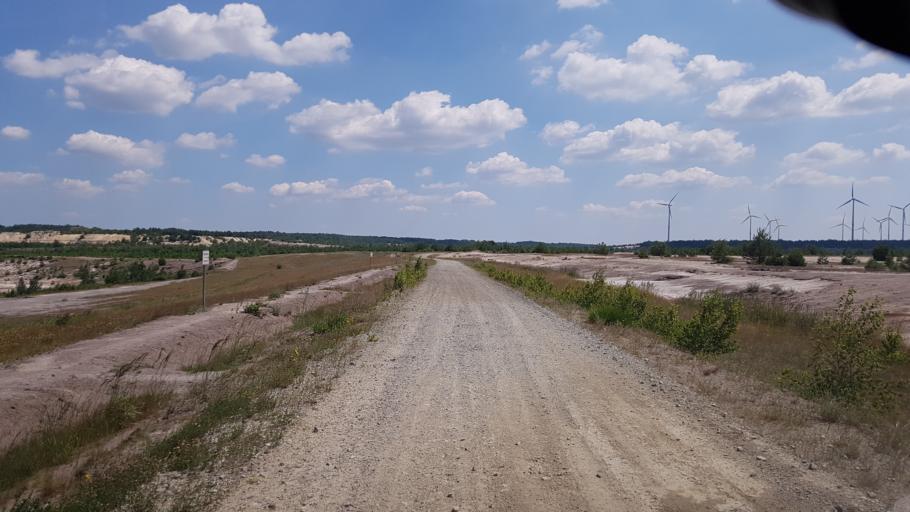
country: DE
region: Brandenburg
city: Sallgast
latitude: 51.5598
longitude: 13.7967
